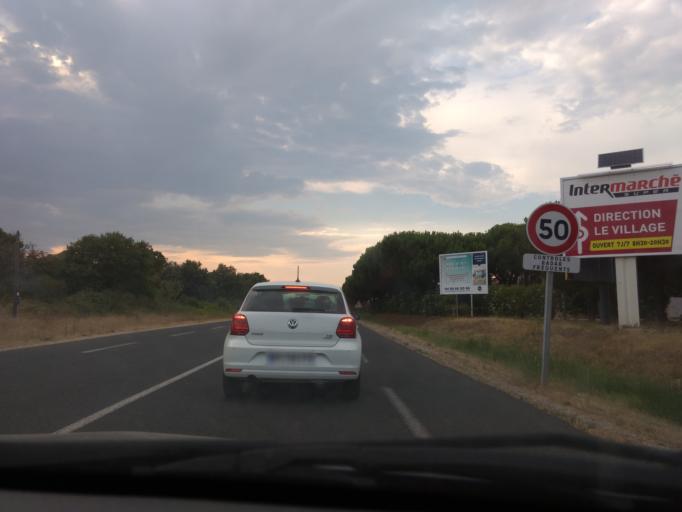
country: FR
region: Languedoc-Roussillon
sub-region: Departement des Pyrenees-Orientales
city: Canet-en-Roussillon
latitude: 42.6895
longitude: 3.0276
